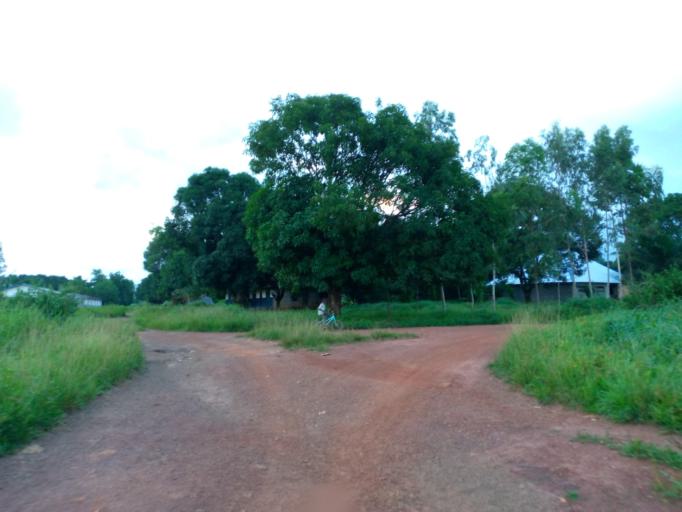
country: SL
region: Northern Province
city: Yonibana
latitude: 8.4611
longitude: -12.2191
